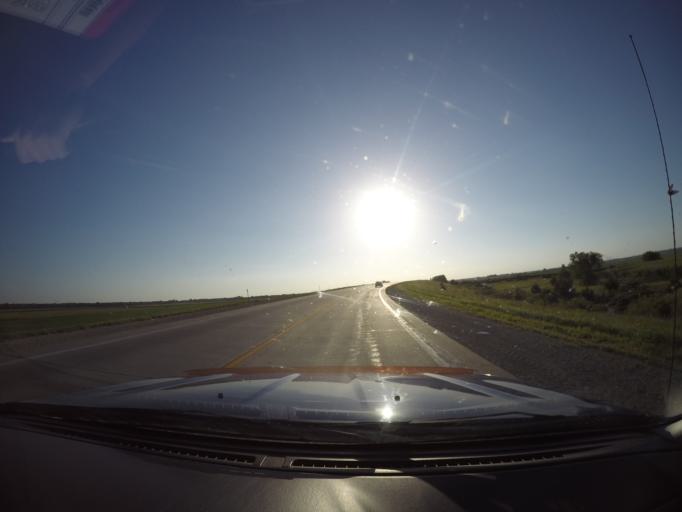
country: US
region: Kansas
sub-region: Pottawatomie County
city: Wamego
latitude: 39.2153
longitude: -96.1951
